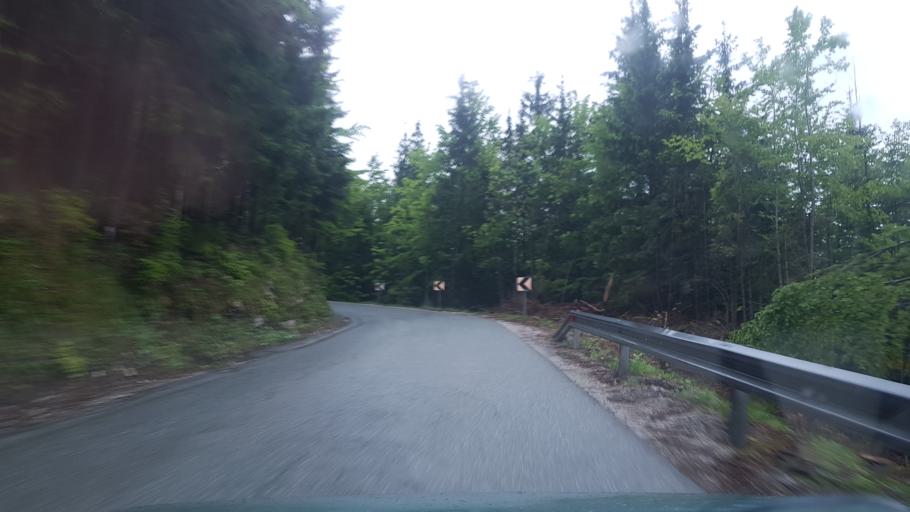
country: SI
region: Bohinj
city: Bohinjska Bistrica
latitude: 46.2681
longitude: 14.0152
